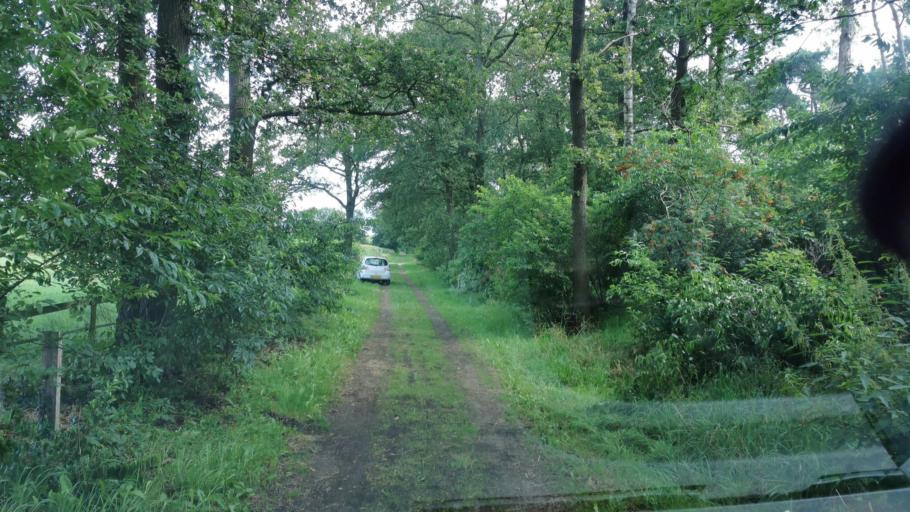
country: NL
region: Overijssel
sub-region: Gemeente Haaksbergen
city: Haaksbergen
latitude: 52.1411
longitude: 6.7529
